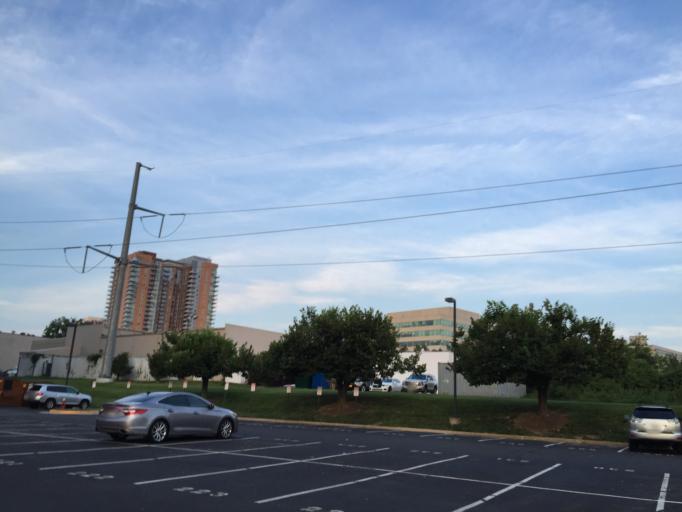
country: US
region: Virginia
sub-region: Fairfax County
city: Tysons Corner
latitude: 38.9268
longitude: -77.2428
